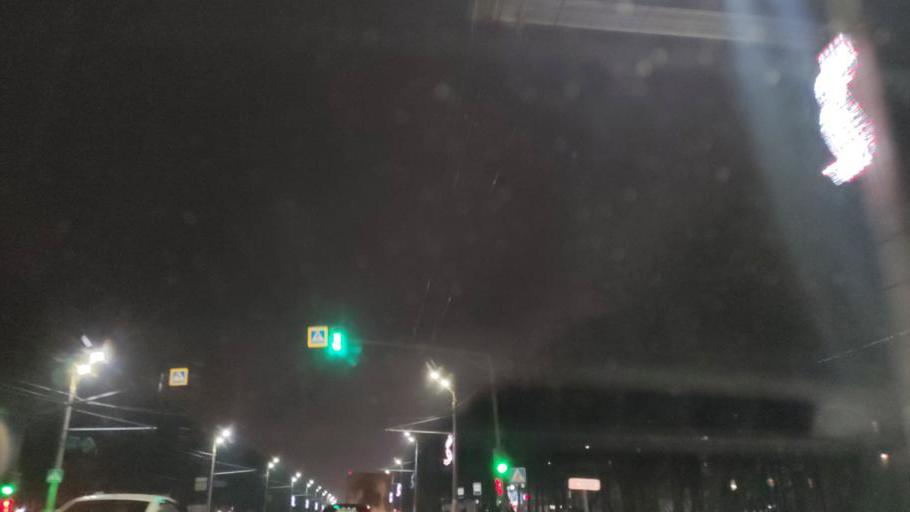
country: RU
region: Moskovskaya
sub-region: Podol'skiy Rayon
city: Podol'sk
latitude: 55.4227
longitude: 37.5187
